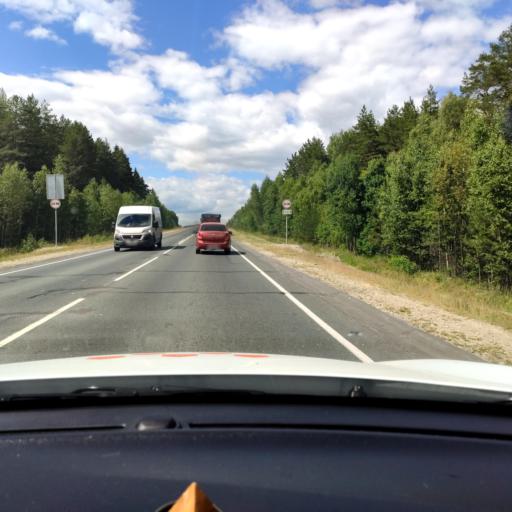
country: RU
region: Mariy-El
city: Volzhsk
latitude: 55.9045
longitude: 48.3799
